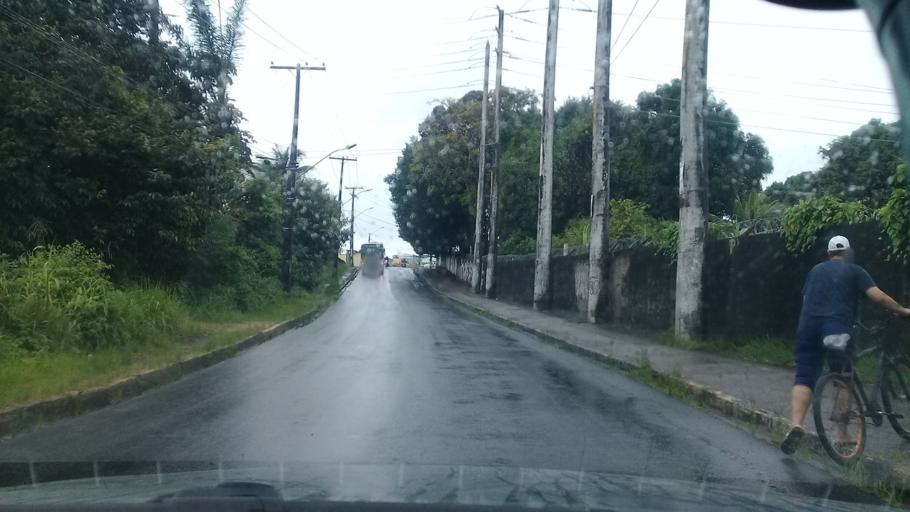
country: BR
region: Pernambuco
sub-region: Jaboatao Dos Guararapes
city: Jaboatao dos Guararapes
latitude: -8.0812
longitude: -34.9803
